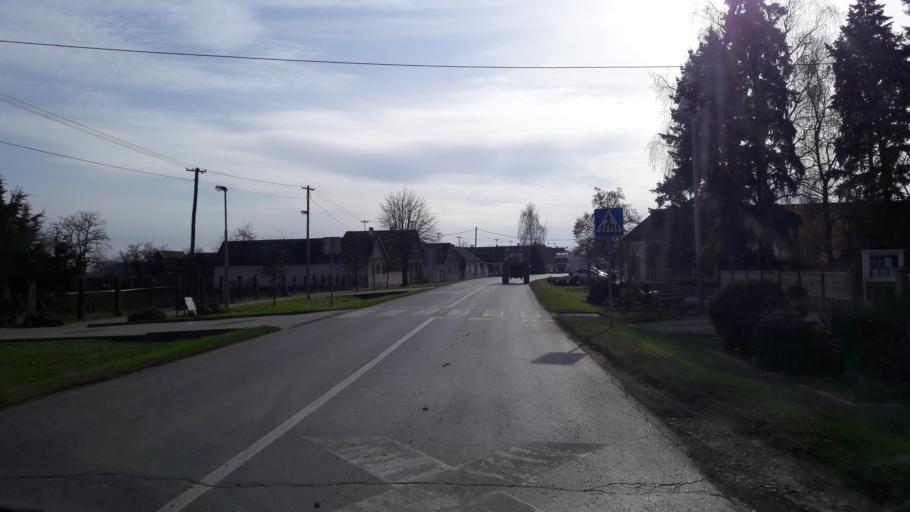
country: HR
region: Osjecko-Baranjska
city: Semeljci
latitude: 45.3055
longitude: 18.5590
